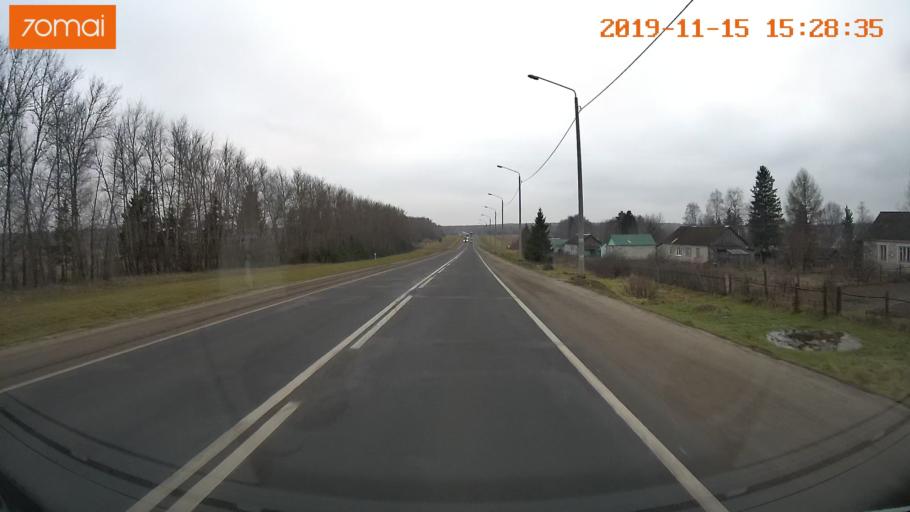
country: RU
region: Jaroslavl
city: Danilov
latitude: 58.1308
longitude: 40.1334
